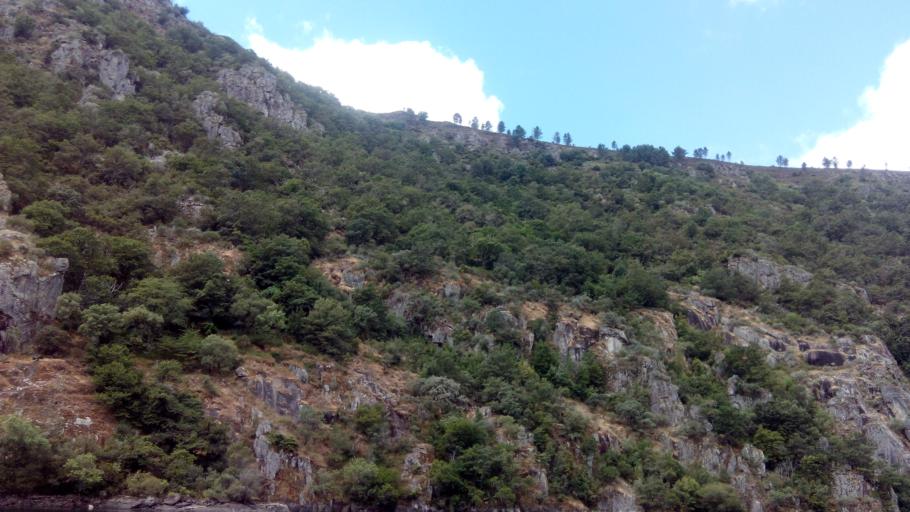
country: ES
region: Galicia
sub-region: Provincia de Lugo
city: Sober
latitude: 42.3955
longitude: -7.6273
